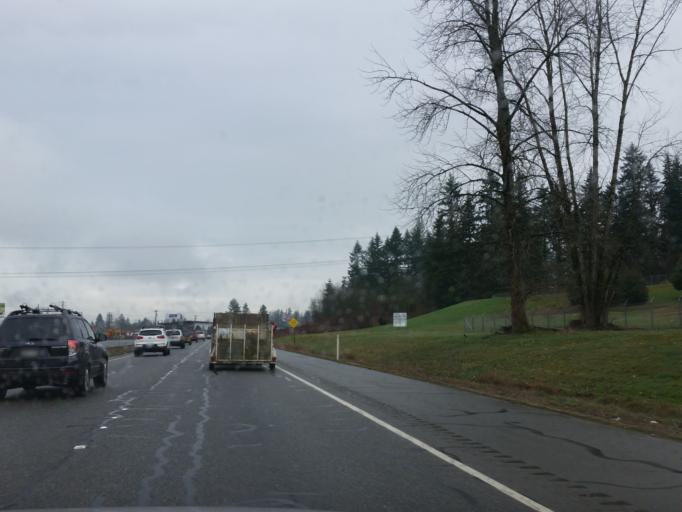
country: US
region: Washington
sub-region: Snohomish County
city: Maltby
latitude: 47.8054
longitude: -122.1102
